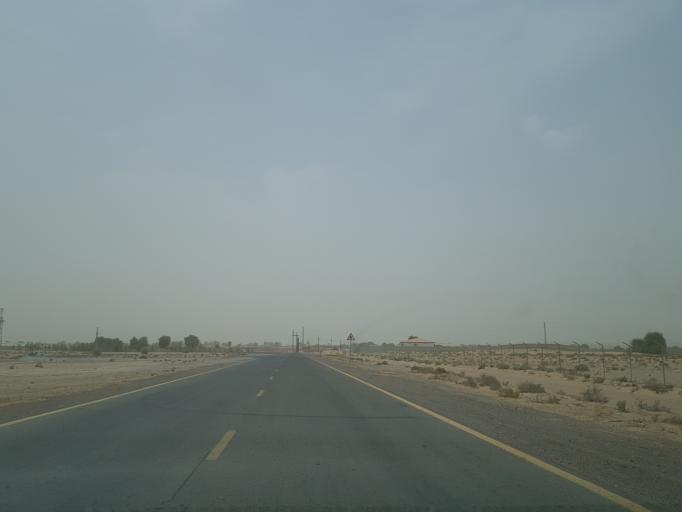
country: AE
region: Dubai
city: Dubai
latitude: 24.9407
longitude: 55.4816
